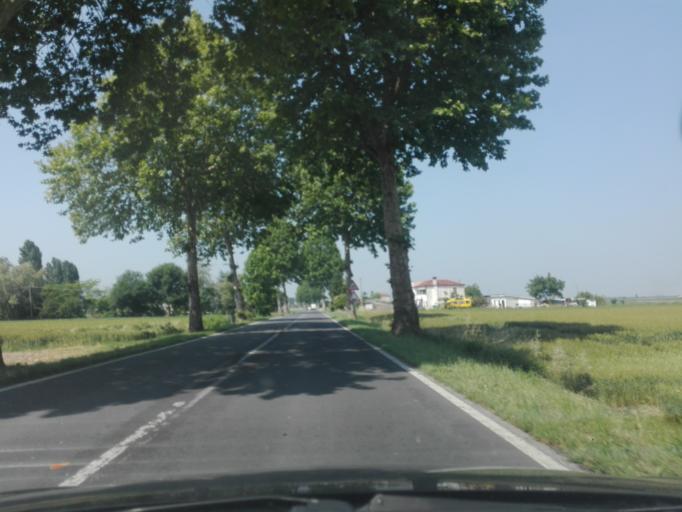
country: IT
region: Veneto
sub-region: Provincia di Rovigo
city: Pettorazza Grimani
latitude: 45.0642
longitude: 11.9792
